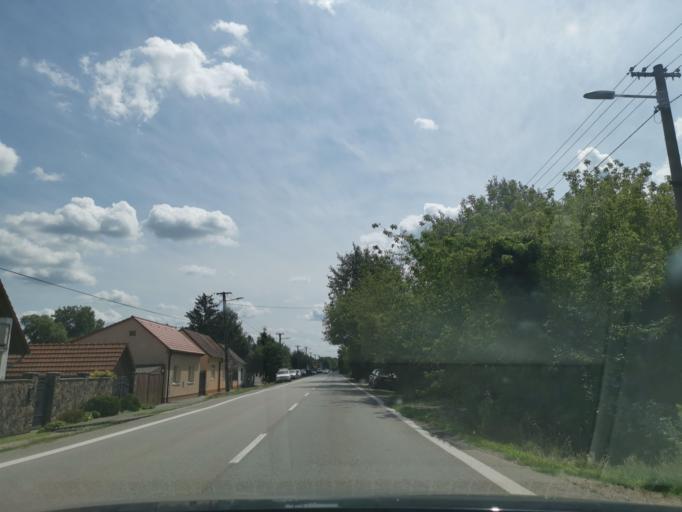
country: SK
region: Bratislavsky
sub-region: Okres Malacky
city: Malacky
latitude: 48.4179
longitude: 17.0197
